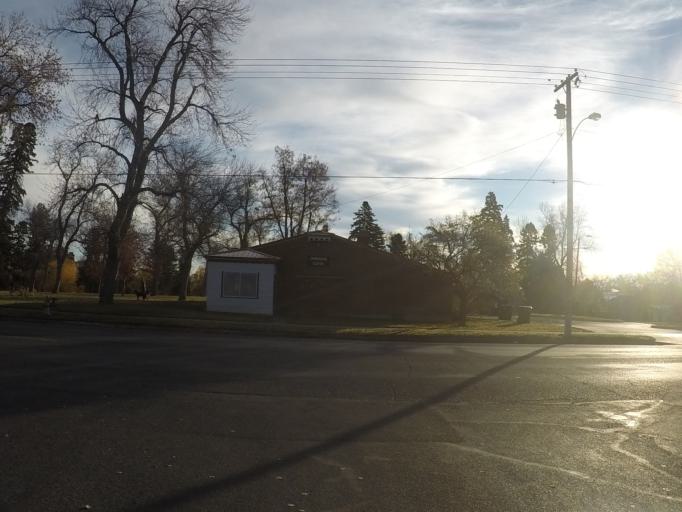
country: US
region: Montana
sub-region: Yellowstone County
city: Billings
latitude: 45.7880
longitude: -108.5281
